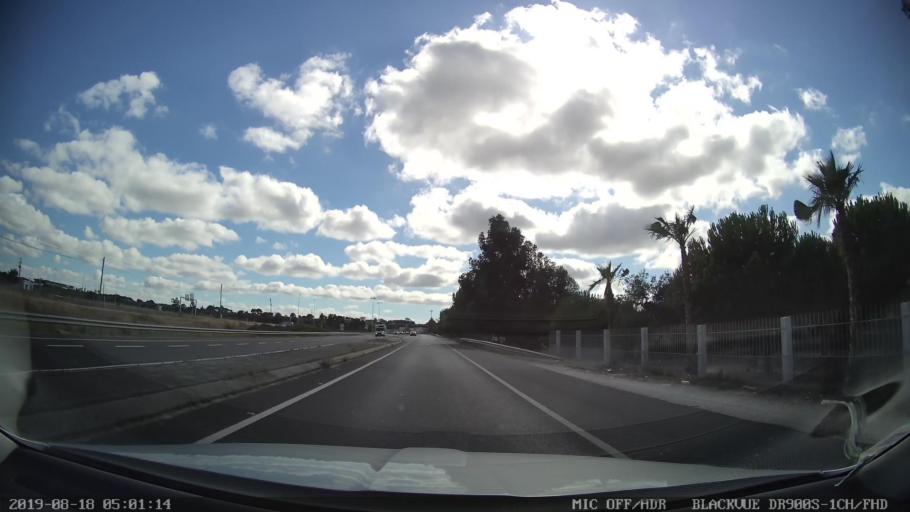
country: PT
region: Santarem
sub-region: Benavente
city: Poceirao
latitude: 38.8431
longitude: -8.7282
